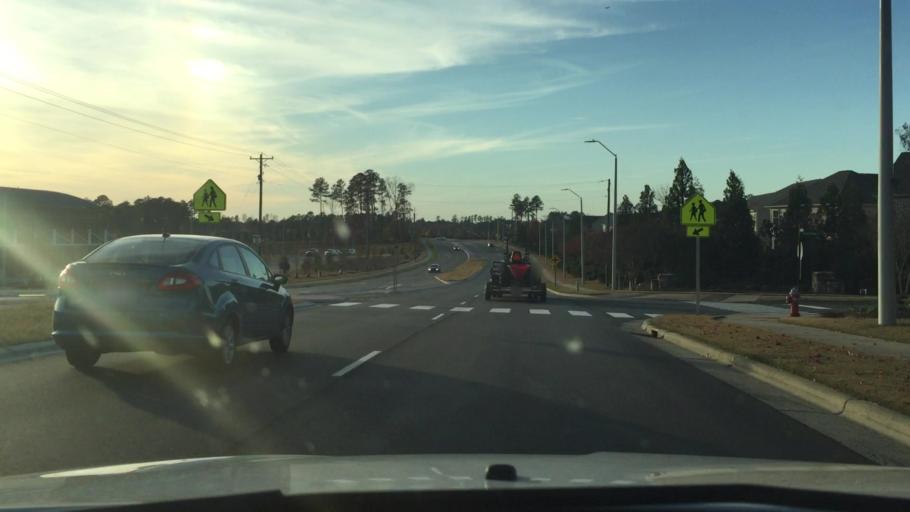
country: US
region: North Carolina
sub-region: Wake County
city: Green Level
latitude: 35.8427
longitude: -78.9055
